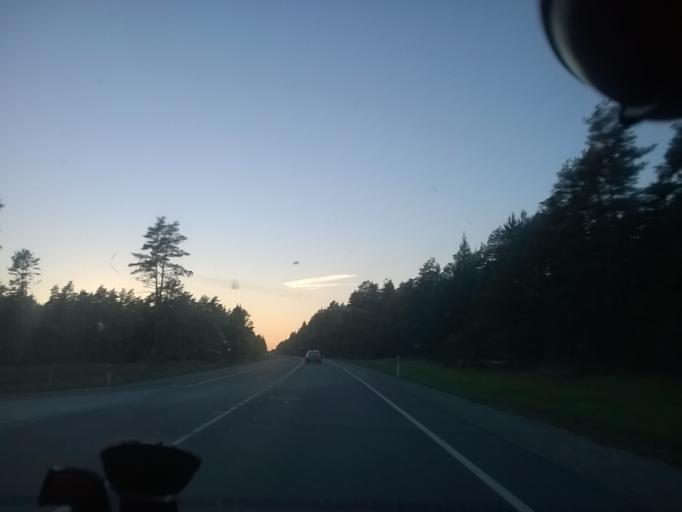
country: EE
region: Laeaene
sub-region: Lihula vald
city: Lihula
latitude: 58.9739
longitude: 23.9278
